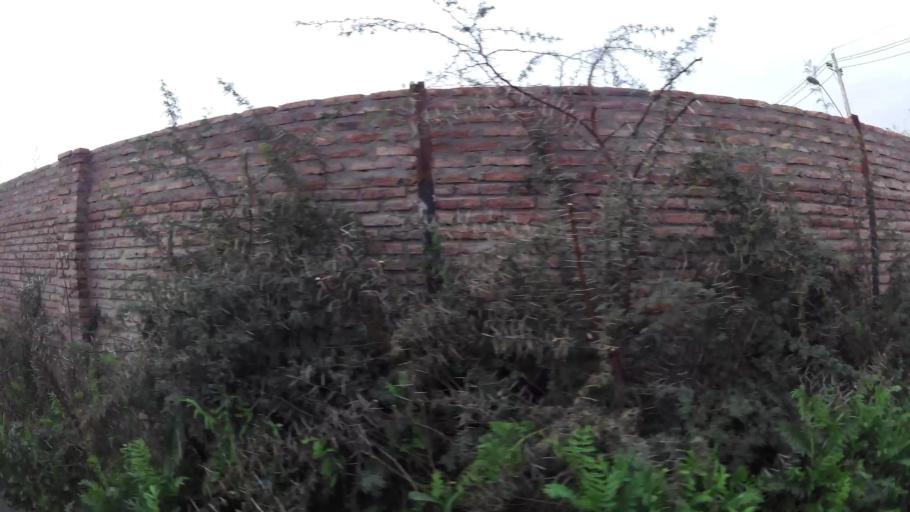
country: CL
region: Santiago Metropolitan
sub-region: Provincia de Chacabuco
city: Chicureo Abajo
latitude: -33.2712
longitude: -70.7078
